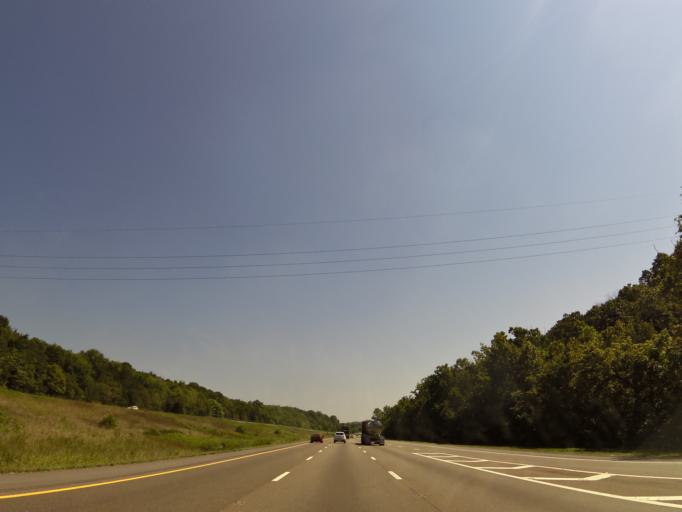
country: US
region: Tennessee
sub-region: Jefferson County
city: New Market
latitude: 36.0090
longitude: -83.5262
